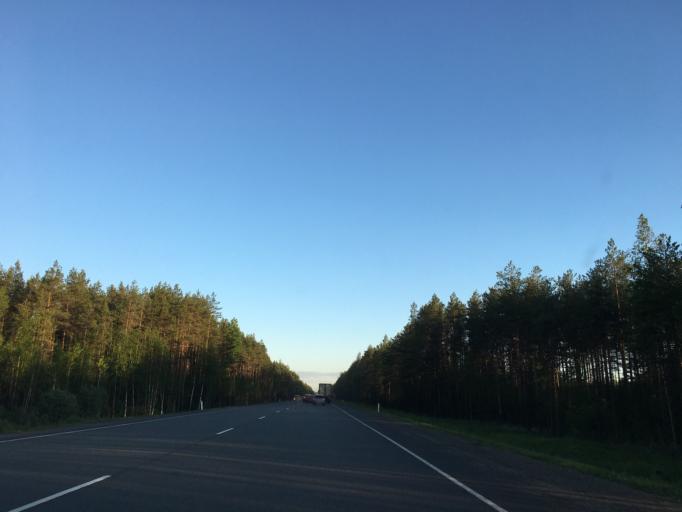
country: RU
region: Leningrad
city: Rozhdestveno
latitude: 59.2961
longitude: 29.9407
